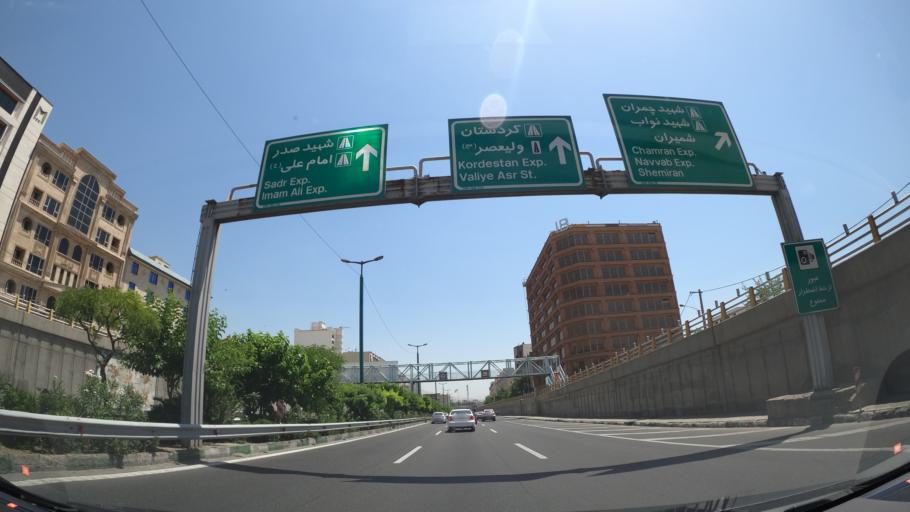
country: IR
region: Tehran
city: Tajrish
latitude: 35.7777
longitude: 51.3805
